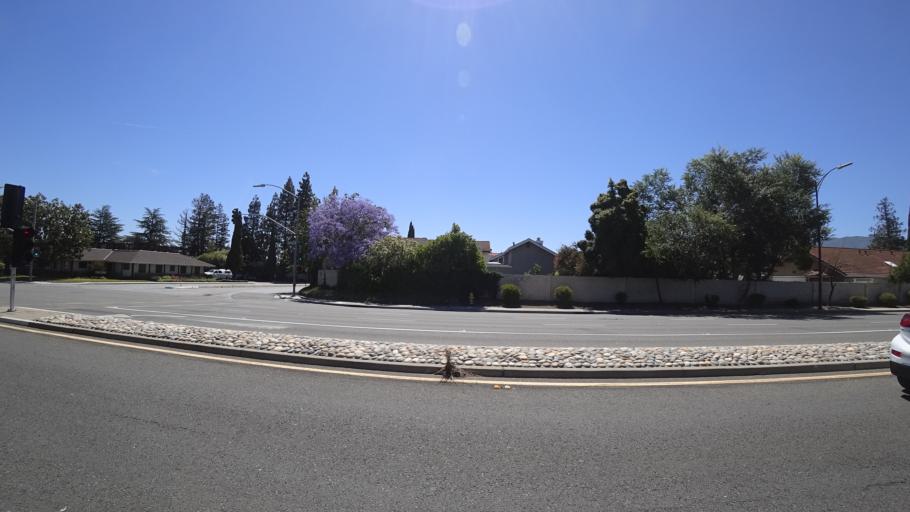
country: US
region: California
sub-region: Santa Clara County
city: Cambrian Park
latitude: 37.2577
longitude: -121.9488
